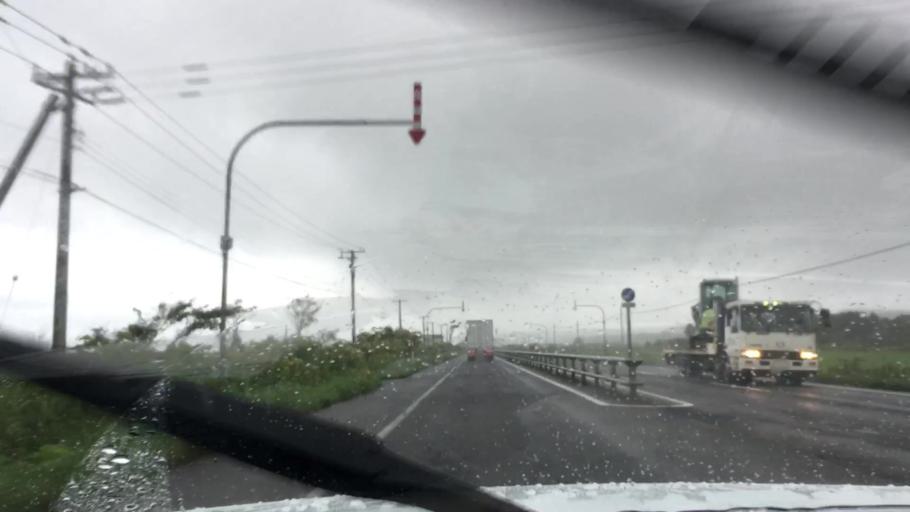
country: JP
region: Hokkaido
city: Niseko Town
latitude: 42.4170
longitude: 140.3107
